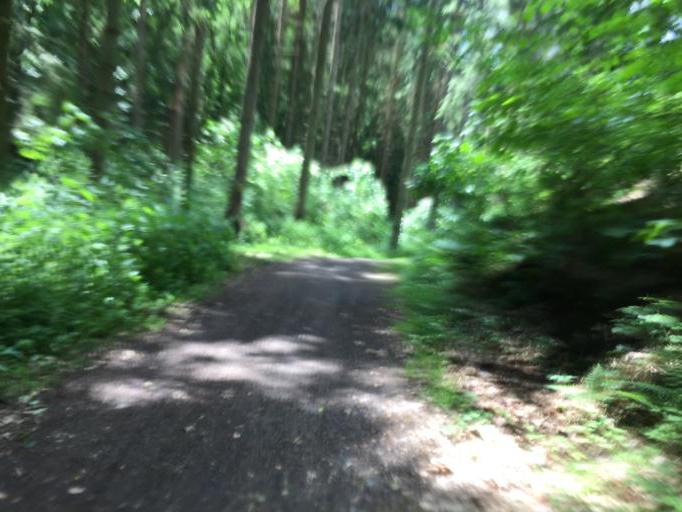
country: DE
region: Rheinland-Pfalz
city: Heilberscheid
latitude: 50.4313
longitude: 7.8739
